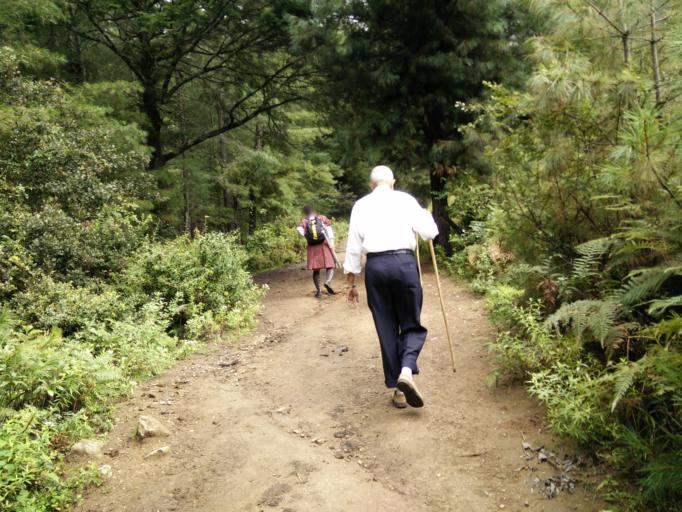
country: BT
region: Paro
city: Paro
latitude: 27.4833
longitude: 89.3611
